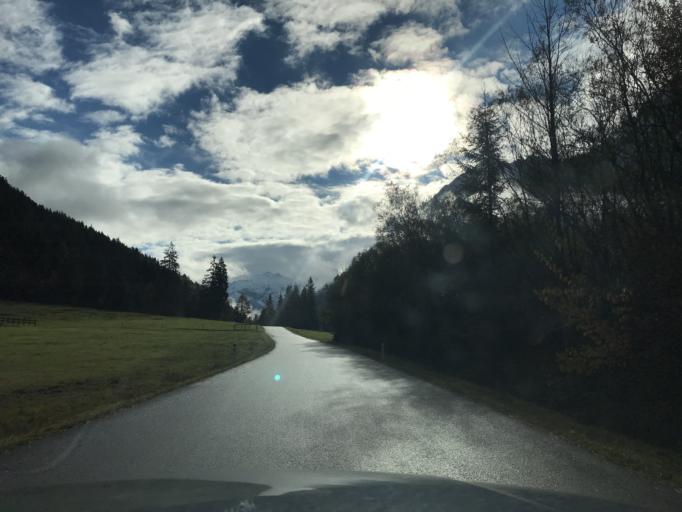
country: DE
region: Bavaria
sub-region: Upper Bavaria
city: Jachenau
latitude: 47.4657
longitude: 11.4924
